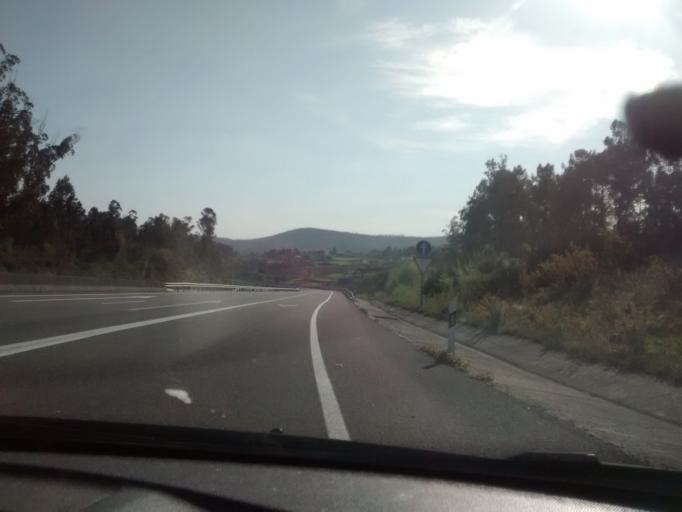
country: ES
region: Galicia
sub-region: Provincia da Coruna
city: Teo
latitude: 42.7976
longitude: -8.5372
